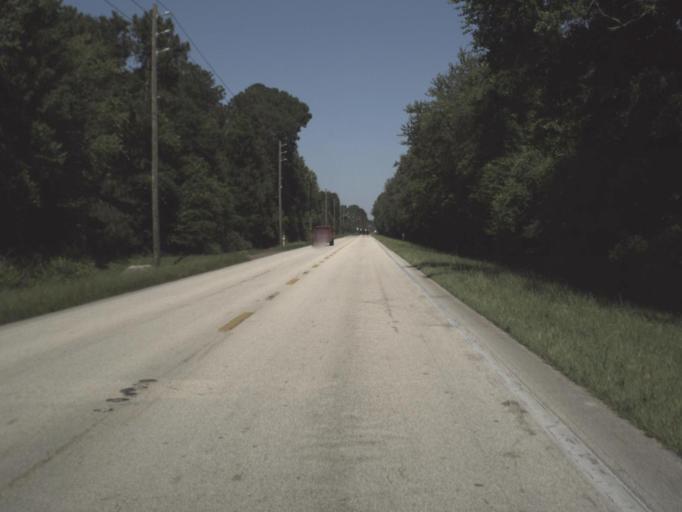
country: US
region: Florida
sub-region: Duval County
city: Baldwin
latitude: 30.3084
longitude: -81.9040
